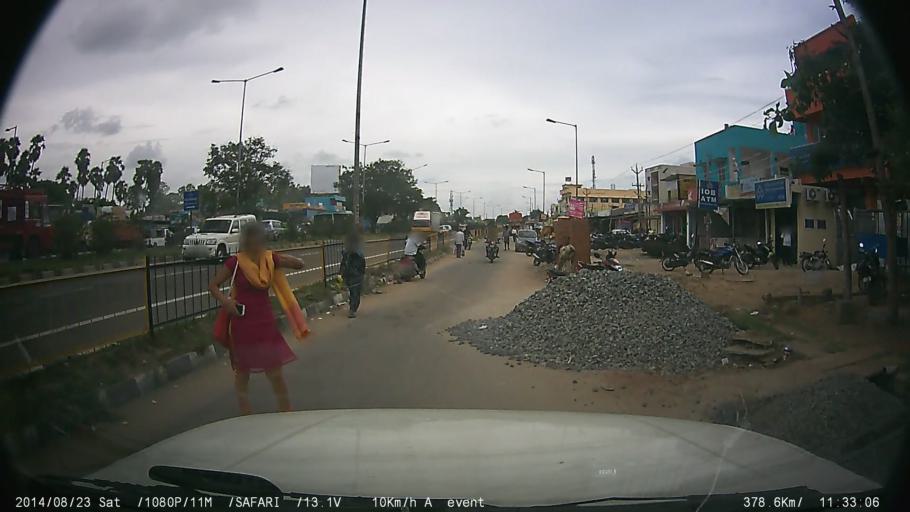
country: IN
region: Tamil Nadu
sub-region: Kancheepuram
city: Singapperumalkovil
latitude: 12.7590
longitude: 80.0028
